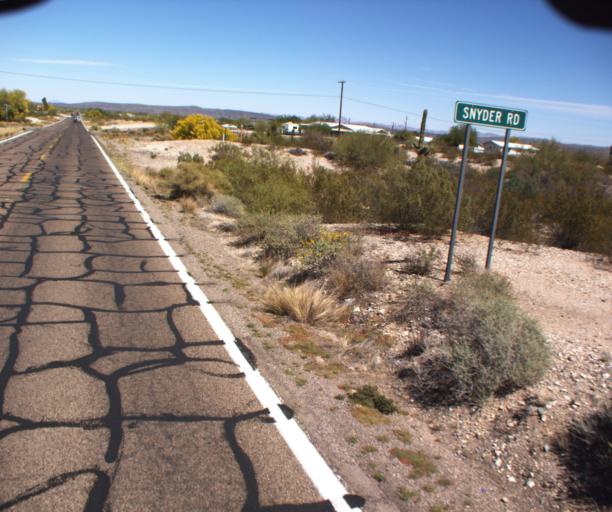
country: US
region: Arizona
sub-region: Pima County
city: Ajo
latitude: 32.3992
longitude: -112.8720
